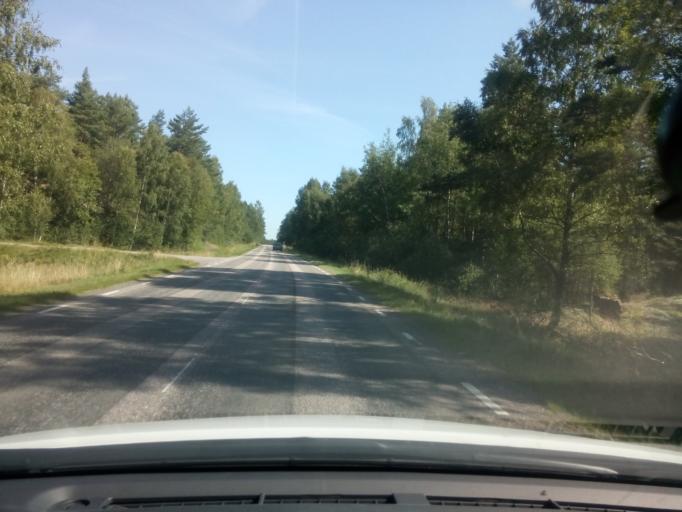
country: SE
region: Soedermanland
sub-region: Oxelosunds Kommun
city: Oxelosund
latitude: 58.7539
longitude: 17.2844
